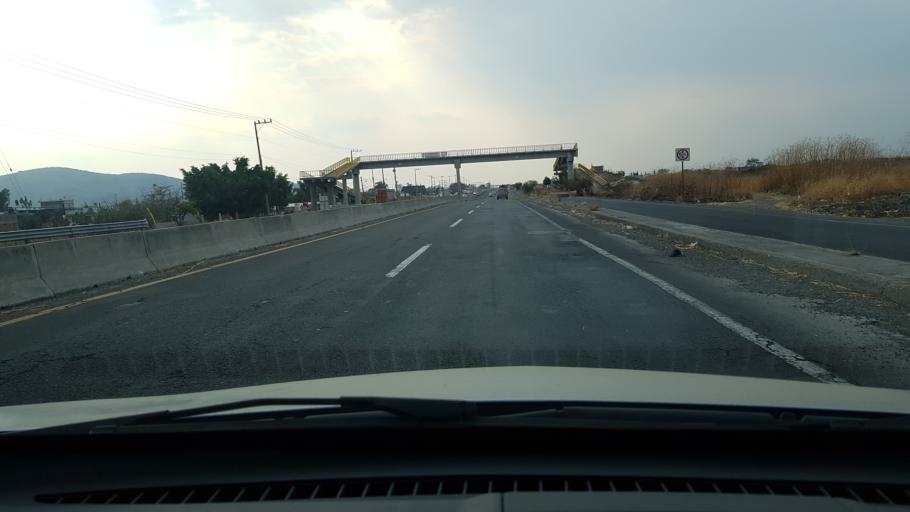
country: MX
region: Morelos
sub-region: Ayala
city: Unidad Habitacional Mariano Matamoros
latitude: 18.7380
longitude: -98.8257
